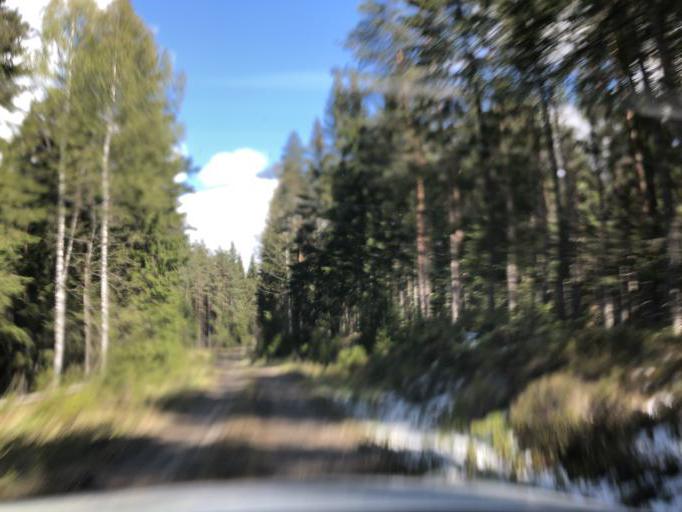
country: SE
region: Dalarna
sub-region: Avesta Kommun
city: Horndal
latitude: 60.2300
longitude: 16.5966
